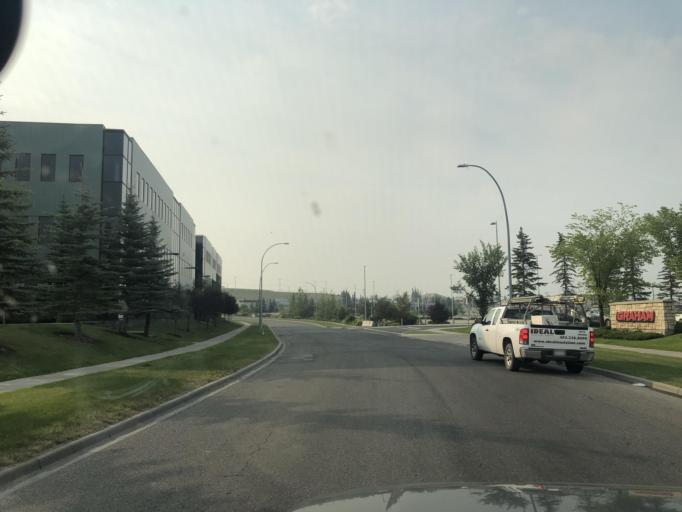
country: CA
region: Alberta
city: Calgary
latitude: 50.9541
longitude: -113.9973
